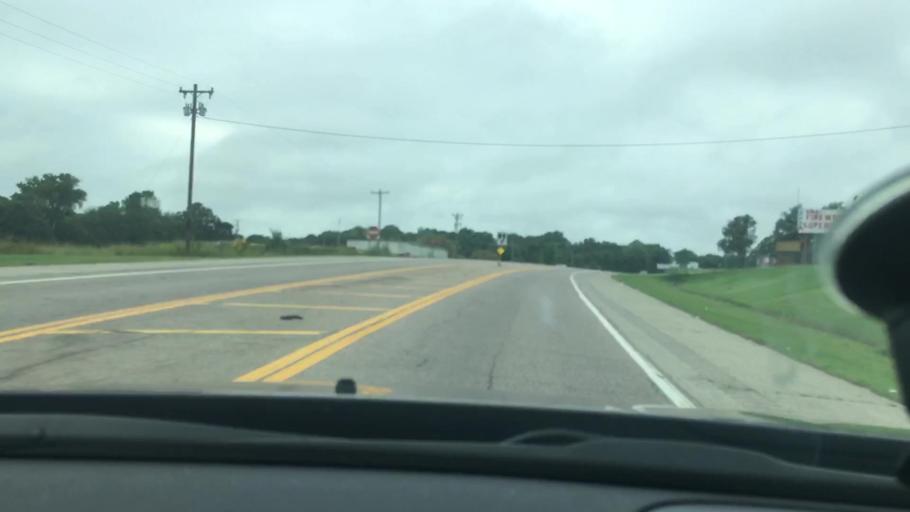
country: US
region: Oklahoma
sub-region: Pontotoc County
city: Ada
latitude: 34.7797
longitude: -96.5828
